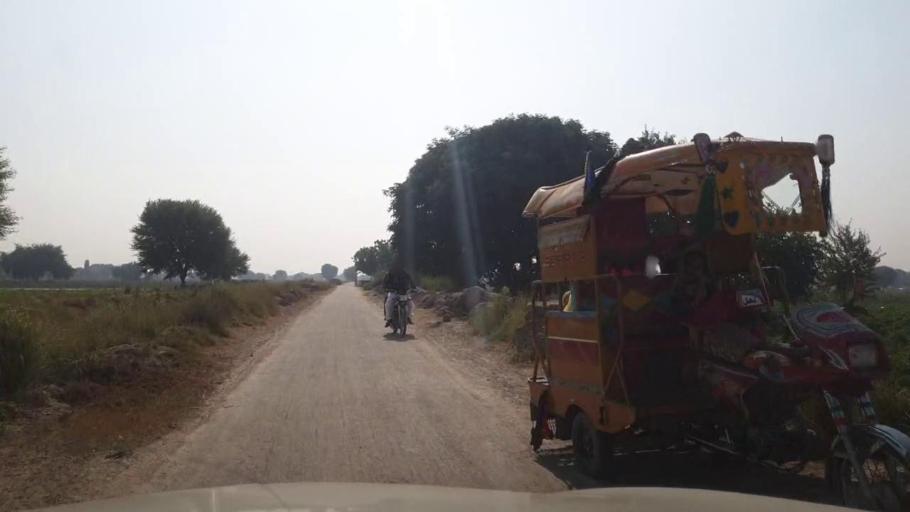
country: PK
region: Sindh
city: Bhan
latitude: 26.5256
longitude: 67.7791
